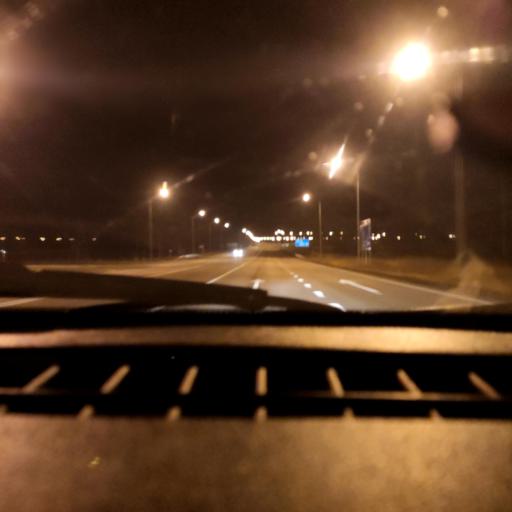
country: RU
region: Bashkortostan
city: Kushnarenkovo
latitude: 55.0645
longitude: 55.4209
